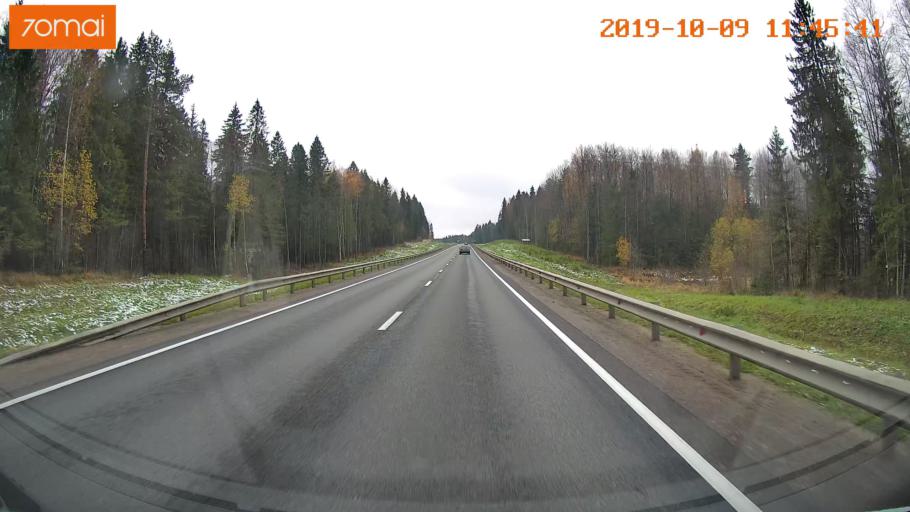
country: RU
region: Vologda
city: Gryazovets
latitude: 58.8650
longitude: 40.1980
